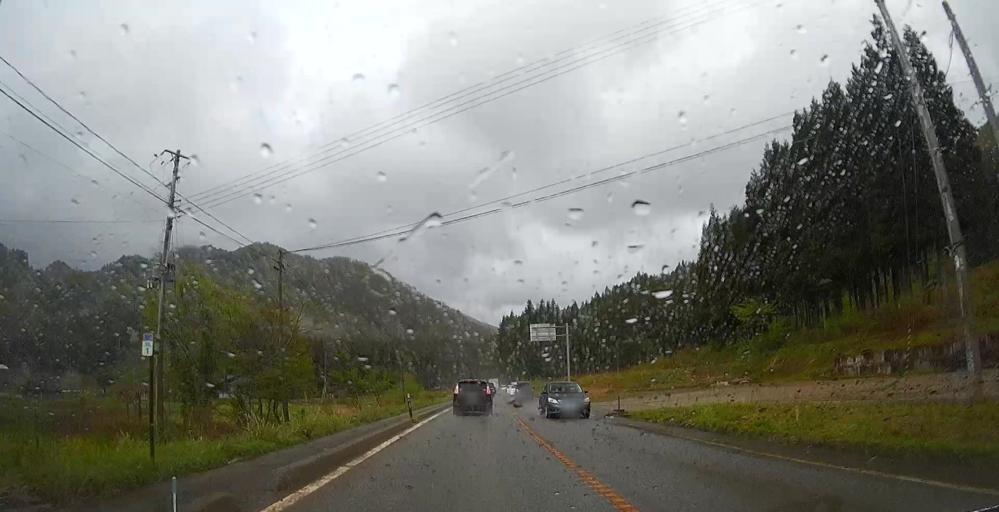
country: JP
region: Yamagata
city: Nagai
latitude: 38.0500
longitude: 139.7947
